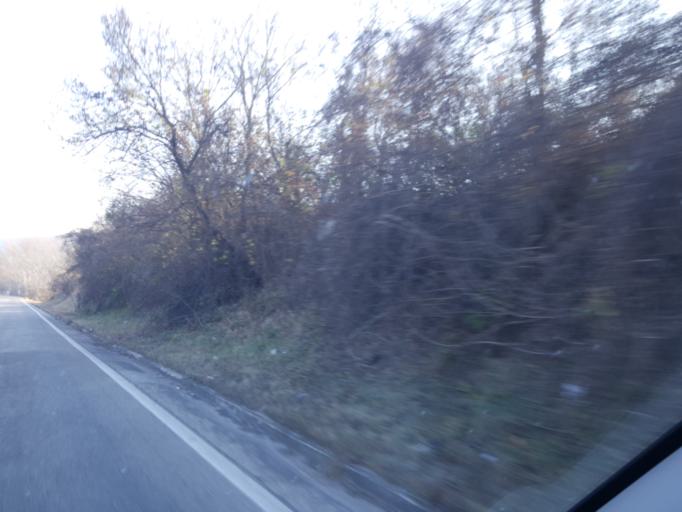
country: RS
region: Central Serbia
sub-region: Pirotski Okrug
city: Bela Palanka
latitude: 43.2830
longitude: 22.2213
